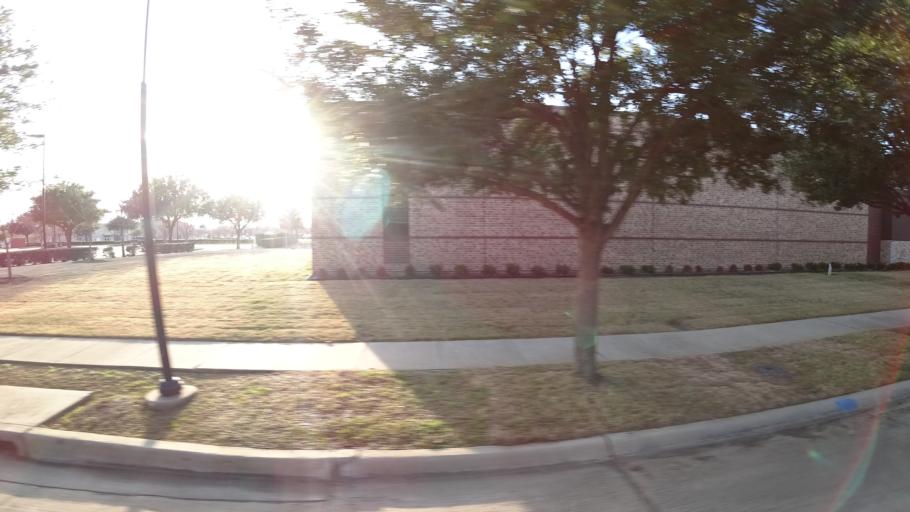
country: US
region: Texas
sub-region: Dallas County
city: Coppell
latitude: 32.9881
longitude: -96.9901
